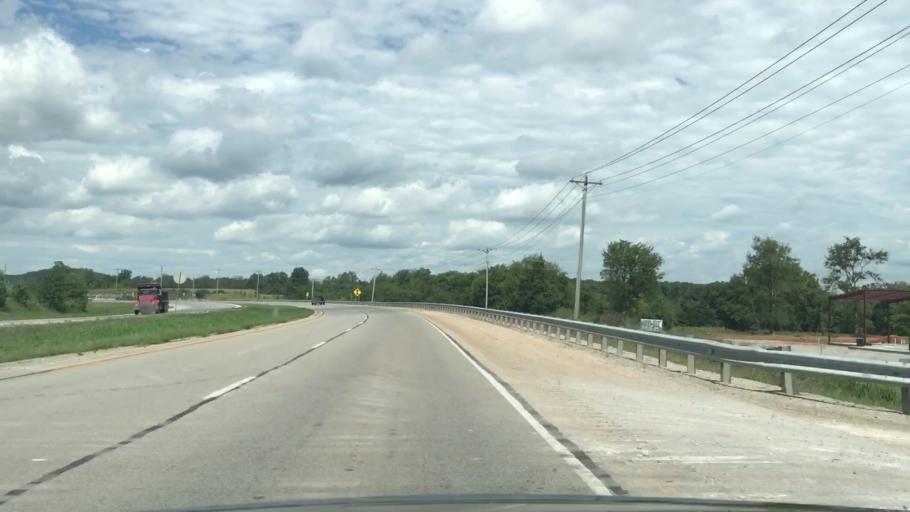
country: US
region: Kentucky
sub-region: Logan County
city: Russellville
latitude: 36.8631
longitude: -86.8647
